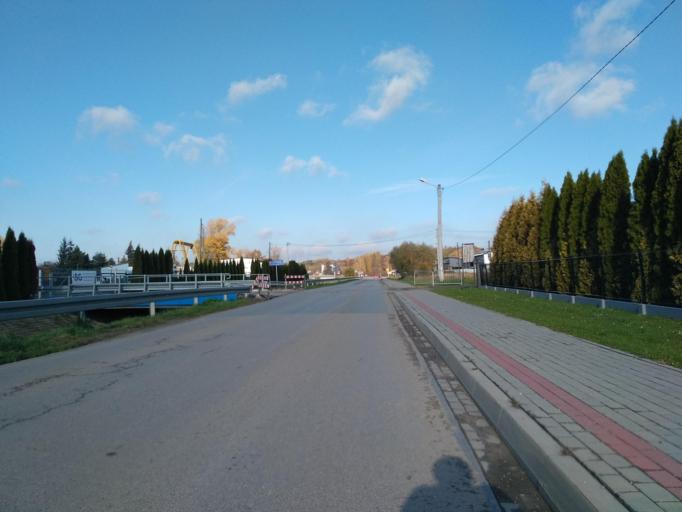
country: PL
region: Subcarpathian Voivodeship
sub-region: Powiat rzeszowski
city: Niechobrz
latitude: 50.0184
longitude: 21.8838
